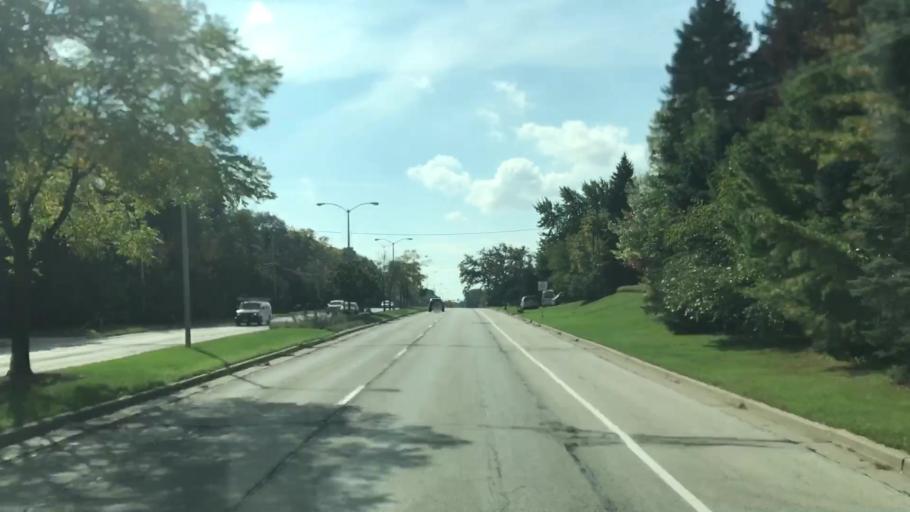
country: US
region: Wisconsin
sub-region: Waukesha County
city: Butler
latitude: 43.1542
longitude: -88.0450
